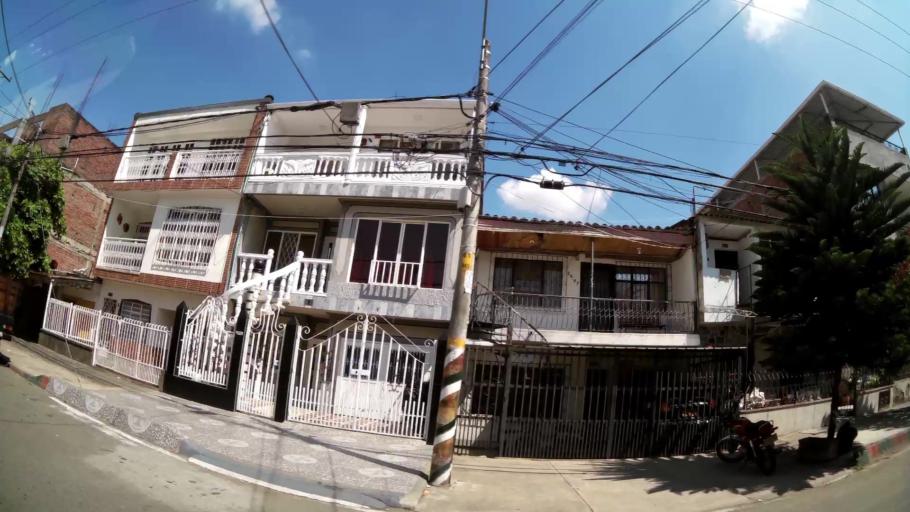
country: CO
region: Valle del Cauca
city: Cali
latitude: 3.4164
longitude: -76.5239
